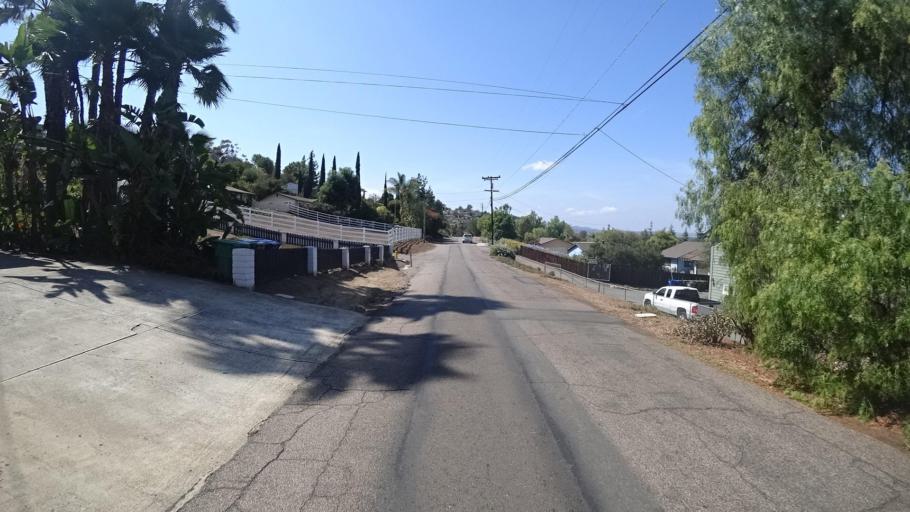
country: US
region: California
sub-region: San Diego County
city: Granite Hills
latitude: 32.7789
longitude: -116.9233
